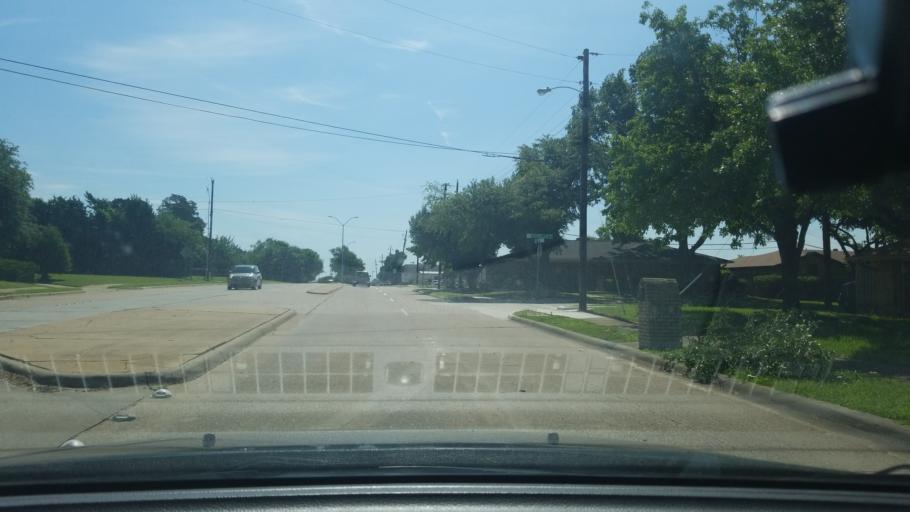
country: US
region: Texas
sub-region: Dallas County
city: Mesquite
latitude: 32.7700
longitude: -96.5916
